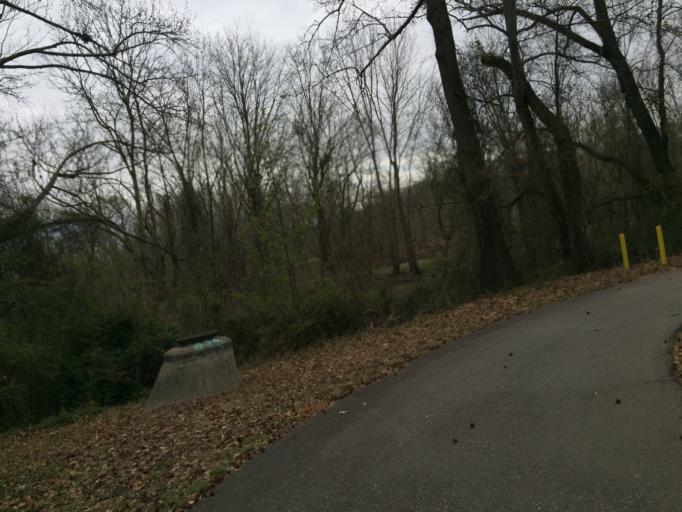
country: US
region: South Carolina
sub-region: Greenville County
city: Mauldin
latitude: 34.7726
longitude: -82.3514
